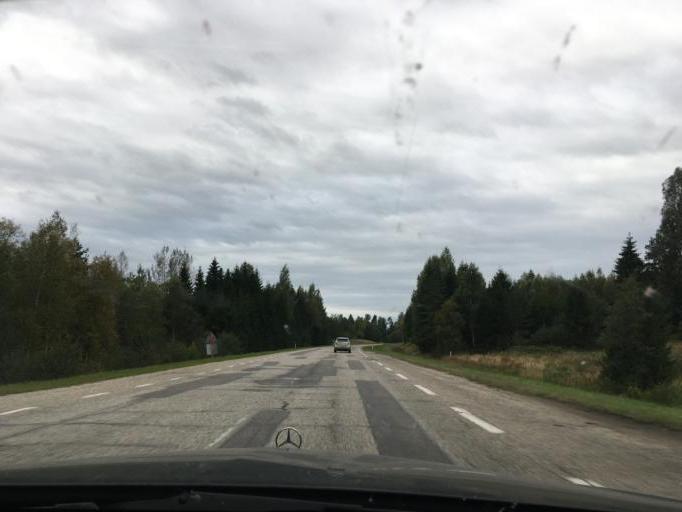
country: LV
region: Aluksnes Rajons
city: Aluksne
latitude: 57.5873
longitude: 27.0748
